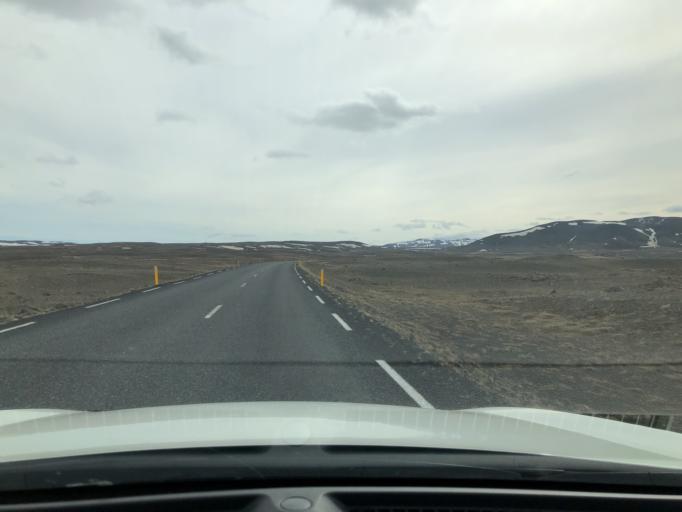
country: IS
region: Northeast
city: Laugar
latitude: 65.5900
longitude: -16.1026
